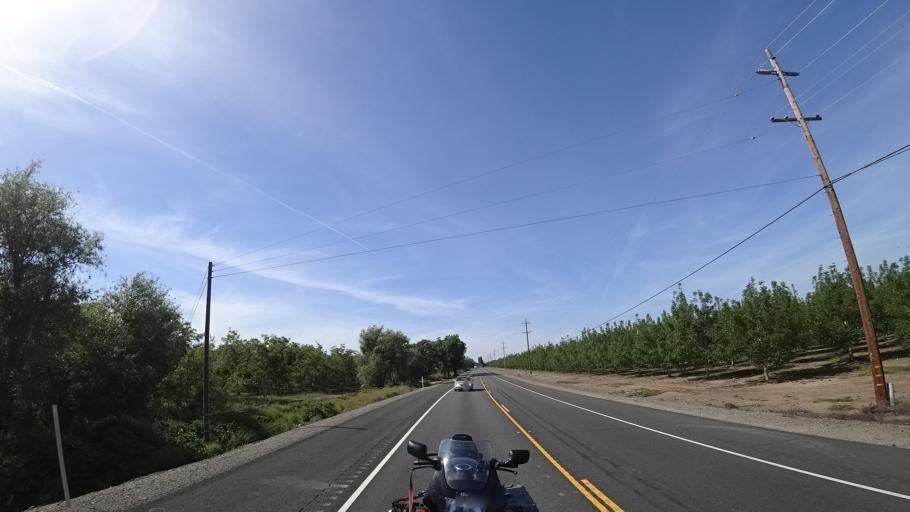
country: US
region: California
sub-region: Glenn County
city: Hamilton City
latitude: 39.8708
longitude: -121.9670
